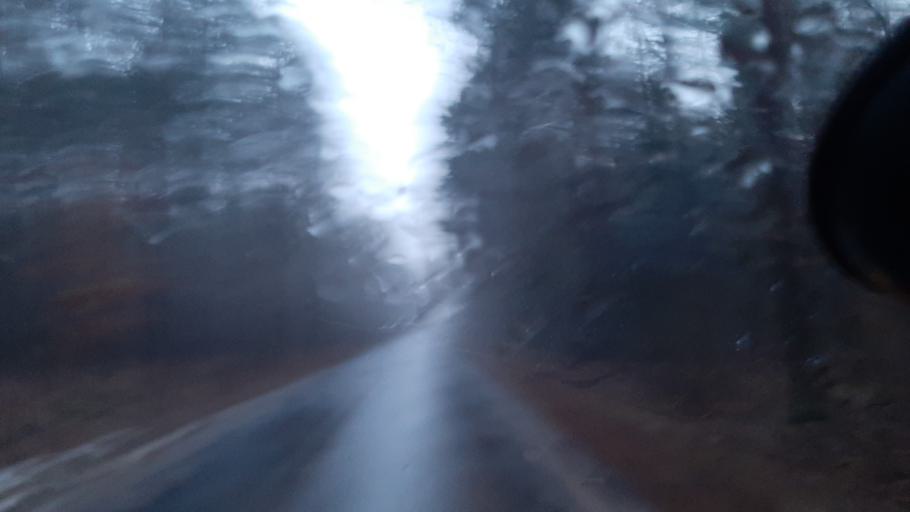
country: PL
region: Lublin Voivodeship
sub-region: Powiat lubartowski
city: Firlej
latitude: 51.5468
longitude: 22.5059
